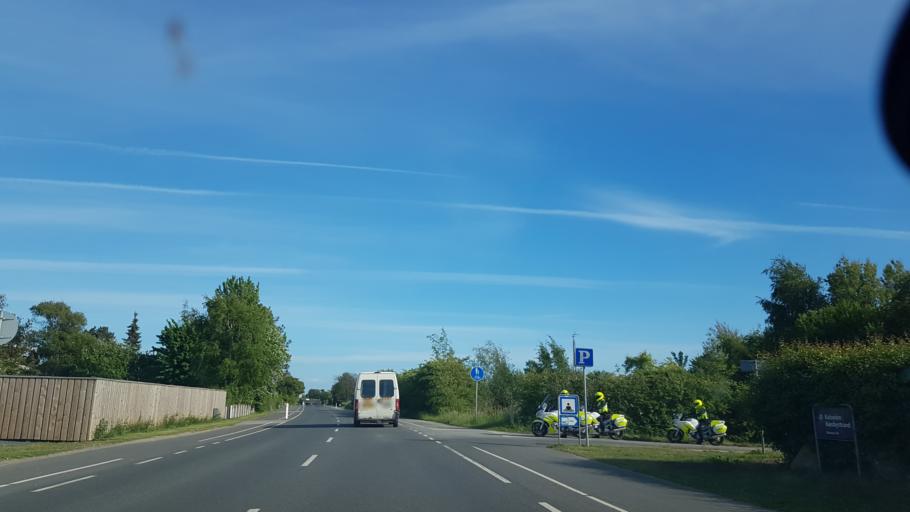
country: DK
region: Zealand
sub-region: Slagelse Kommune
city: Forlev
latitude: 55.3990
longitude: 11.2183
